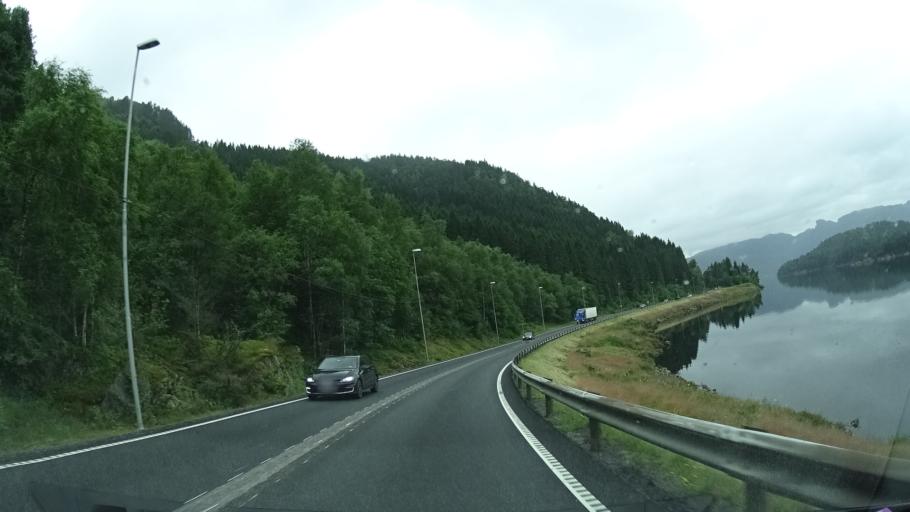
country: NO
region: Rogaland
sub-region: Lund
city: Moi
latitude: 58.4406
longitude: 6.6109
